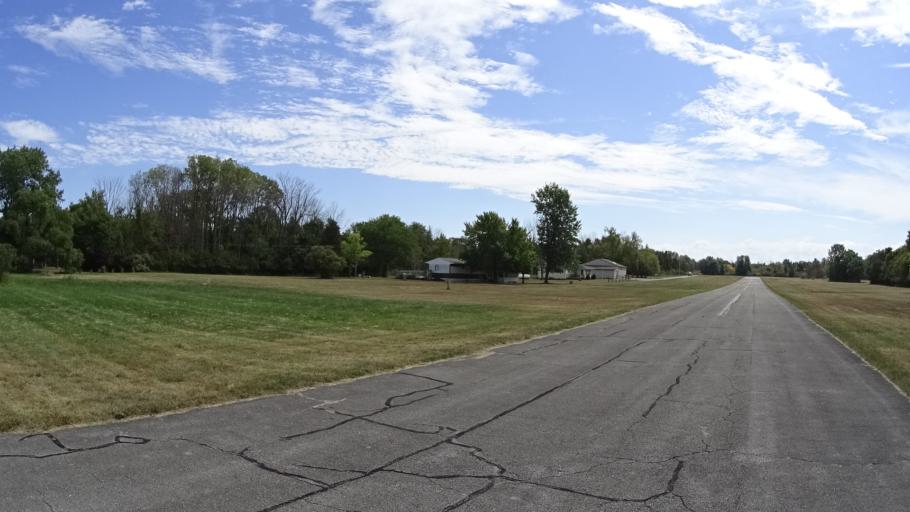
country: US
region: Ohio
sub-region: Erie County
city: Sandusky
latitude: 41.6030
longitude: -82.6872
